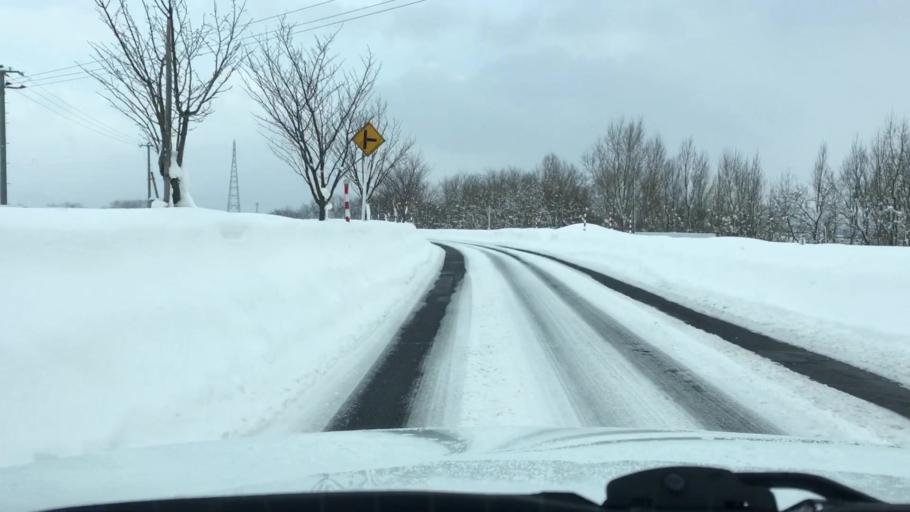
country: JP
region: Aomori
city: Hirosaki
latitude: 40.6503
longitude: 140.4732
